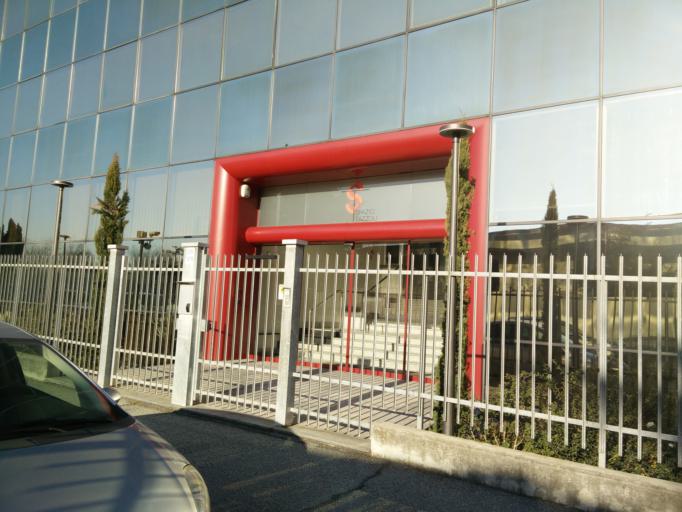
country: IT
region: Piedmont
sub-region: Provincia di Torino
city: Gerbido
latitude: 45.0359
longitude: 7.6170
